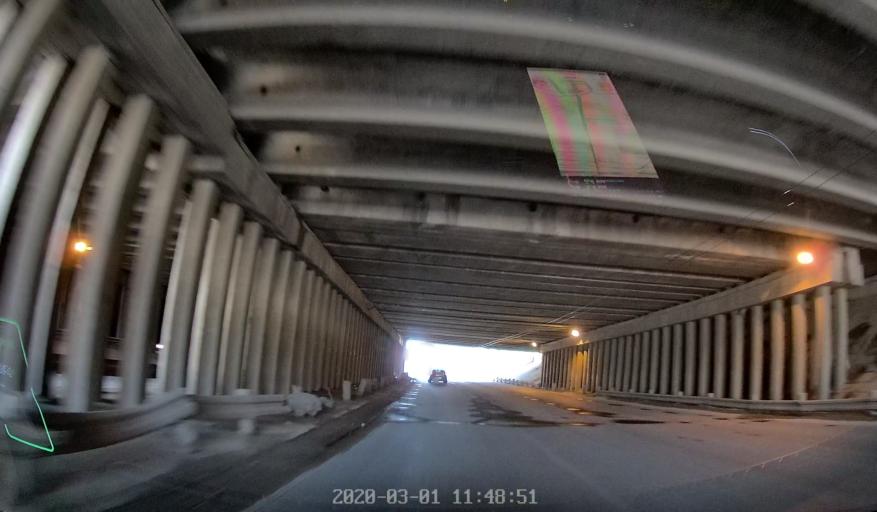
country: GR
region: South Aegean
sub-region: Nomos Kykladon
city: Serifos
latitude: 37.1731
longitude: 24.5487
